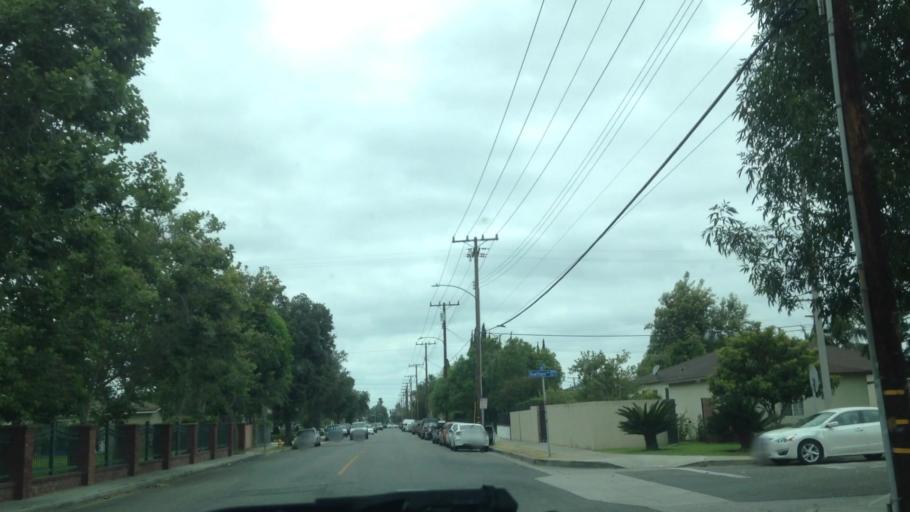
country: US
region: California
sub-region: Orange County
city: Anaheim
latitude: 33.8434
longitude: -117.9000
